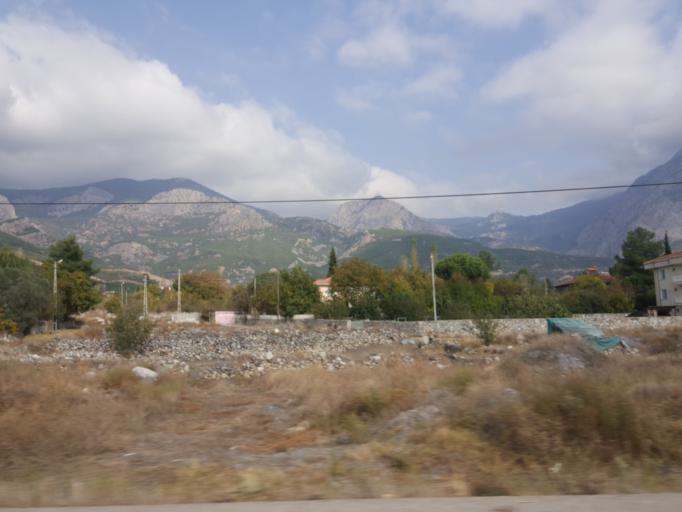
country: TR
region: Corum
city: Kargi
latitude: 41.1333
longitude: 34.4386
